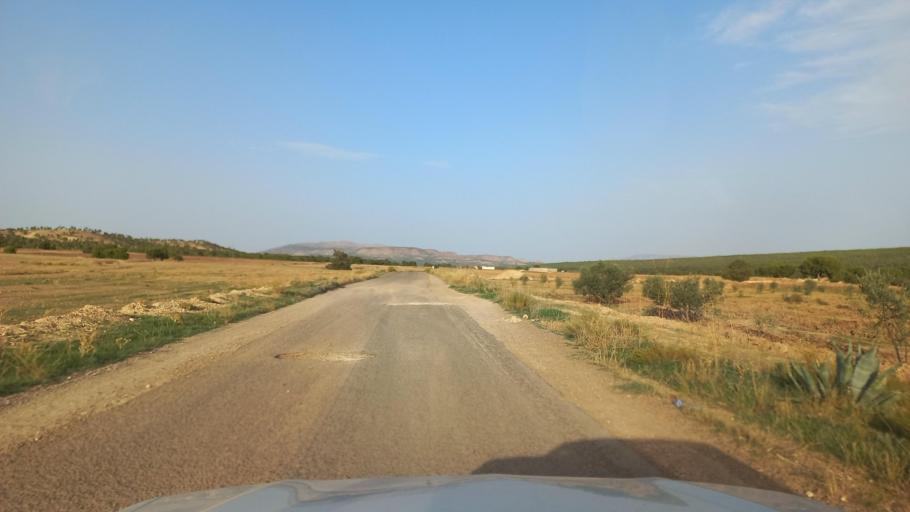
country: TN
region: Al Qasrayn
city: Kasserine
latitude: 35.3947
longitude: 8.8771
